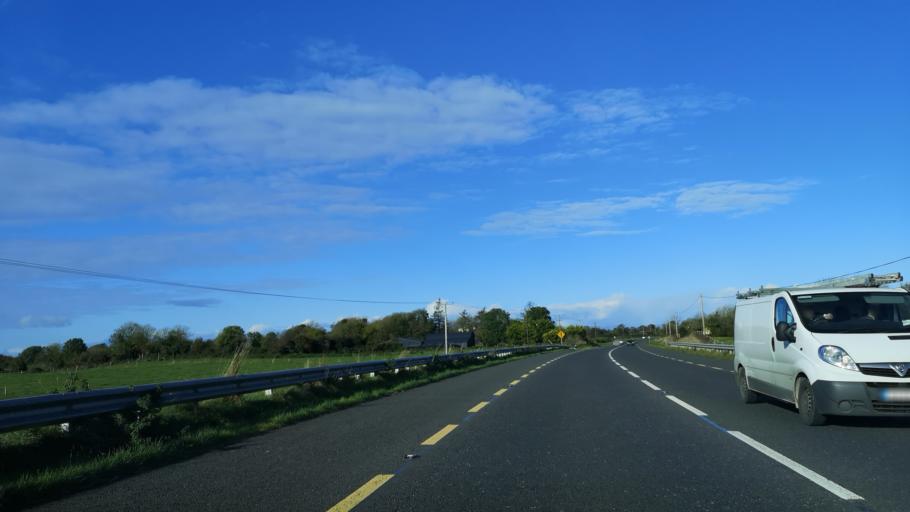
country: IE
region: Connaught
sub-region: County Galway
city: Moycullen
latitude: 53.4400
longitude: -9.0757
